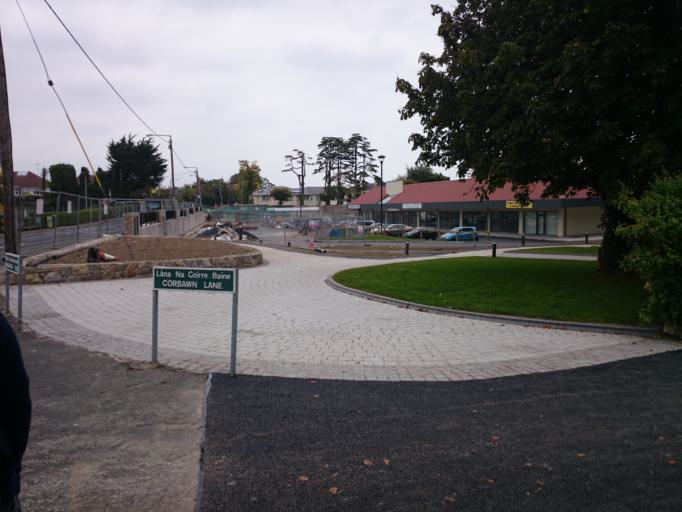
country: IE
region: Leinster
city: Shankill
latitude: 53.2333
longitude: -6.1234
